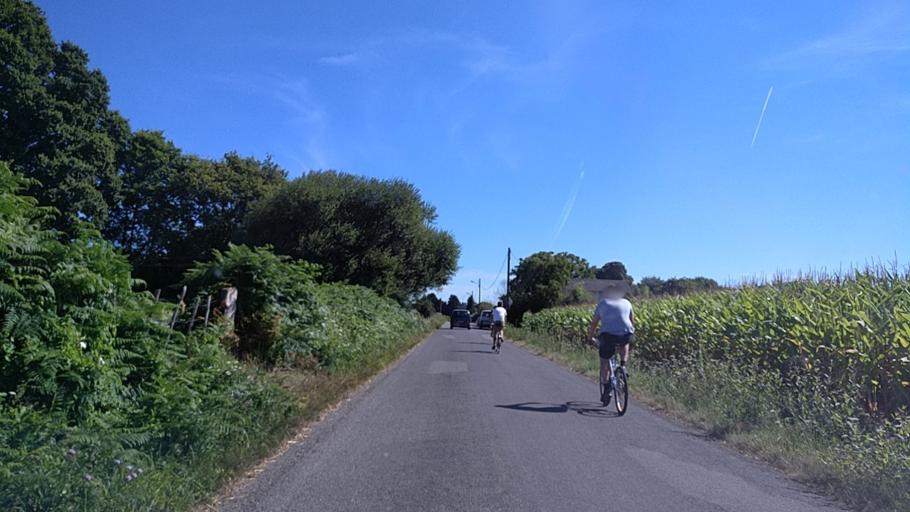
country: FR
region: Brittany
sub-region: Departement d'Ille-et-Vilaine
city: Plerguer
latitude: 48.5221
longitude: -1.8578
